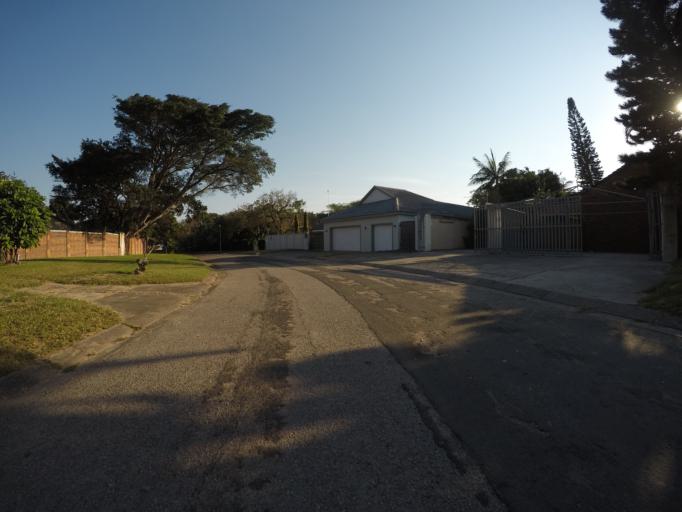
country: ZA
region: KwaZulu-Natal
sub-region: uThungulu District Municipality
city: Richards Bay
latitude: -28.7753
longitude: 32.1043
